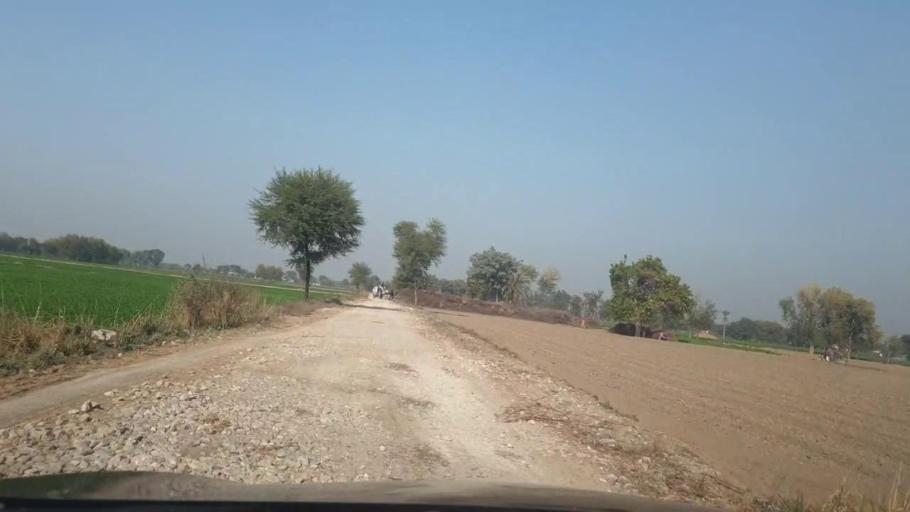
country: PK
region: Sindh
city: Ubauro
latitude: 28.0884
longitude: 69.8411
